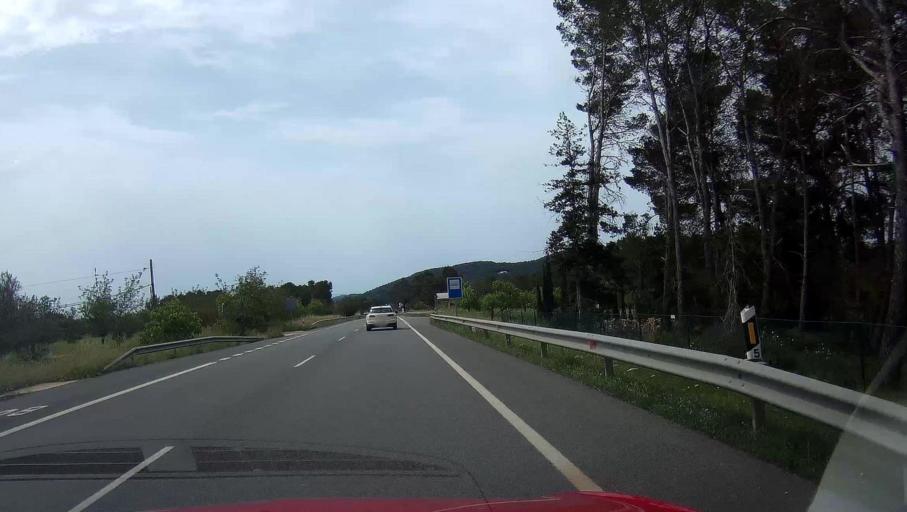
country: ES
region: Balearic Islands
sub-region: Illes Balears
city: Sant Joan de Labritja
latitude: 39.0594
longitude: 1.4941
